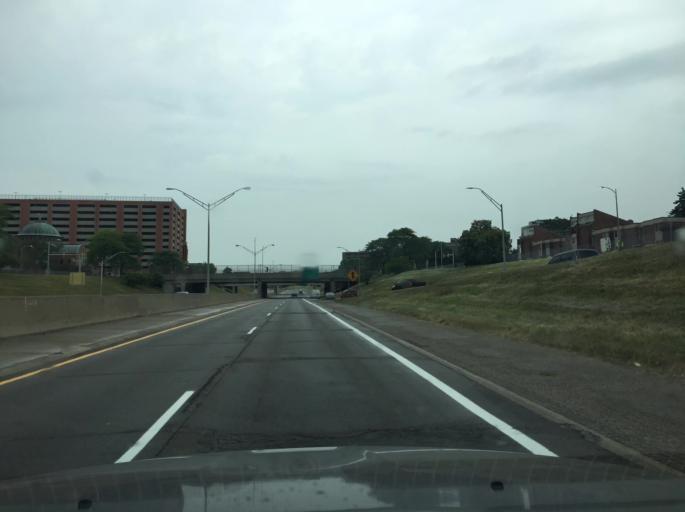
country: US
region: Michigan
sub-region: Wayne County
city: Detroit
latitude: 42.3343
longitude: -83.0368
